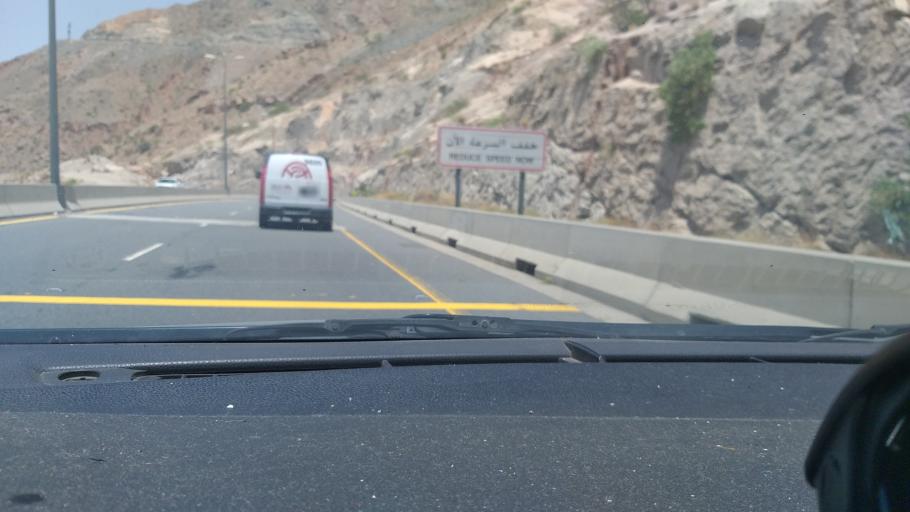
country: SA
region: Makkah
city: Al Hada
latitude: 21.3409
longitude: 40.2563
